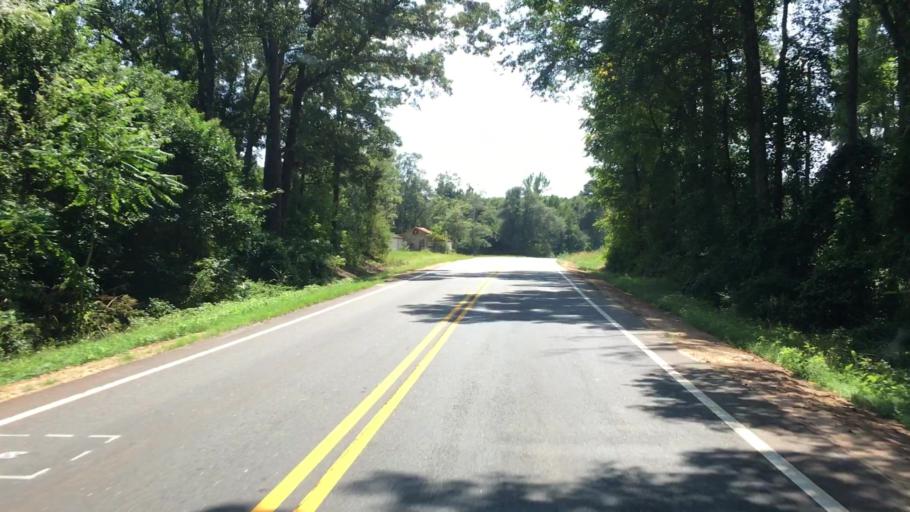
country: US
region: Georgia
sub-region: Oconee County
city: Watkinsville
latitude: 33.7730
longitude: -83.4275
